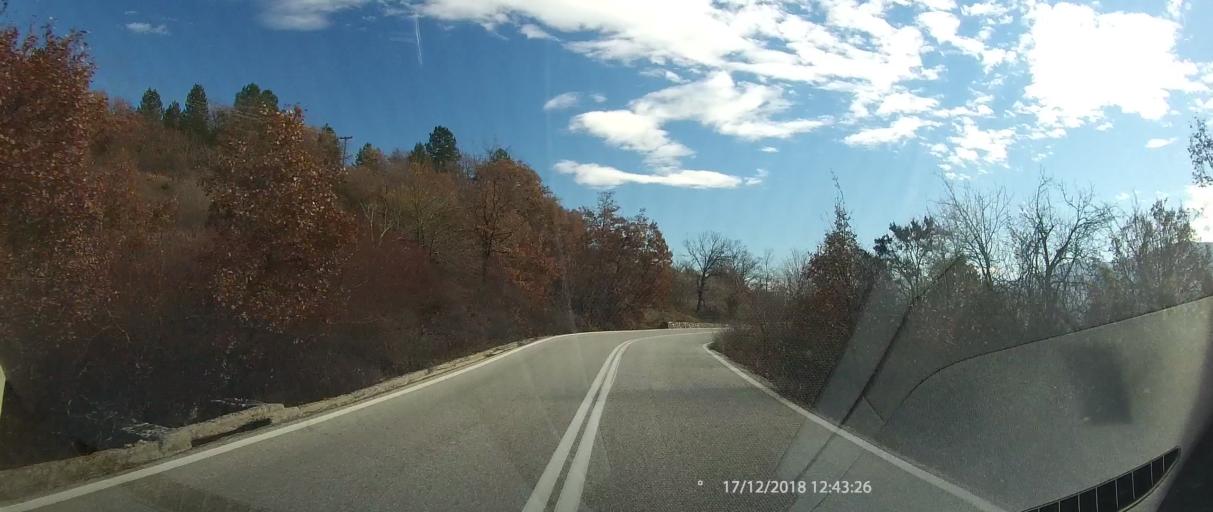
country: GR
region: Epirus
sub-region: Nomos Ioanninon
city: Metsovo
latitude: 39.7838
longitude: 21.3891
